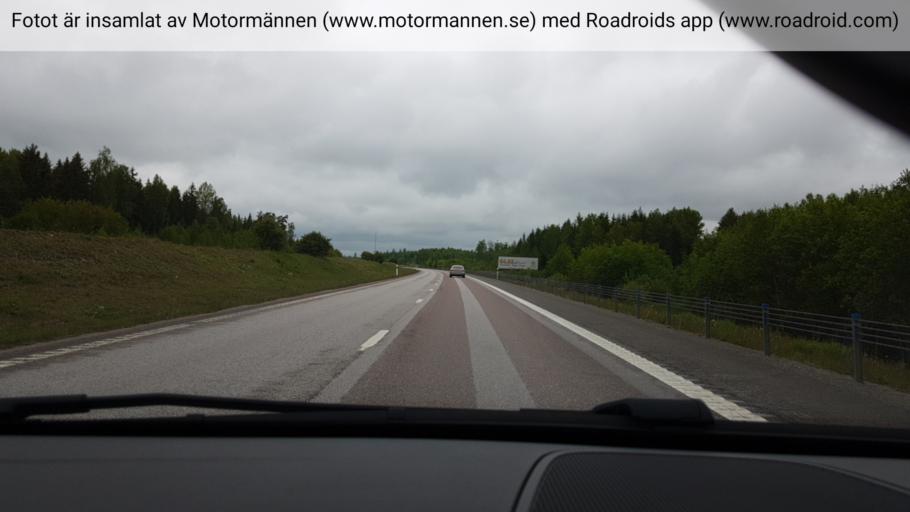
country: SE
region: Uppsala
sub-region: Osthammars Kommun
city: Bjorklinge
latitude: 60.0318
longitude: 17.6294
